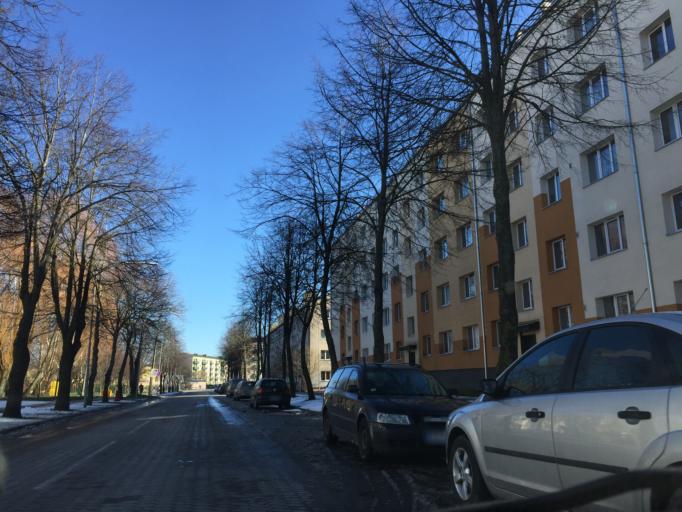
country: LV
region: Ventspils
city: Ventspils
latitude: 57.3912
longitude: 21.5707
